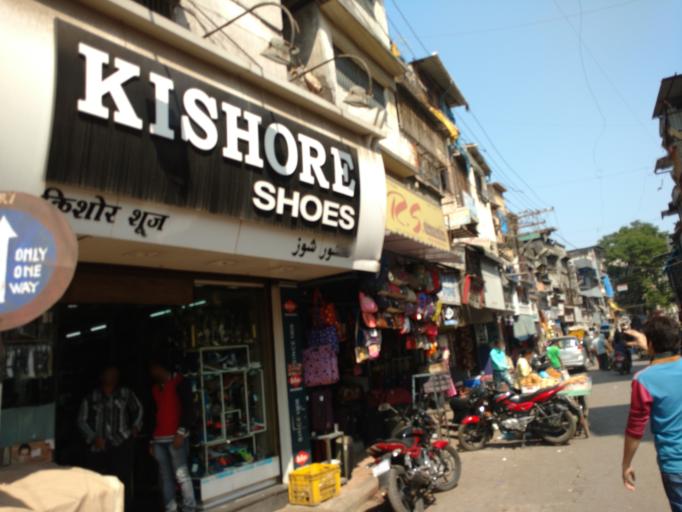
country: IN
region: Maharashtra
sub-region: Thane
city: Ulhasnagar
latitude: 19.2336
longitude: 73.1620
